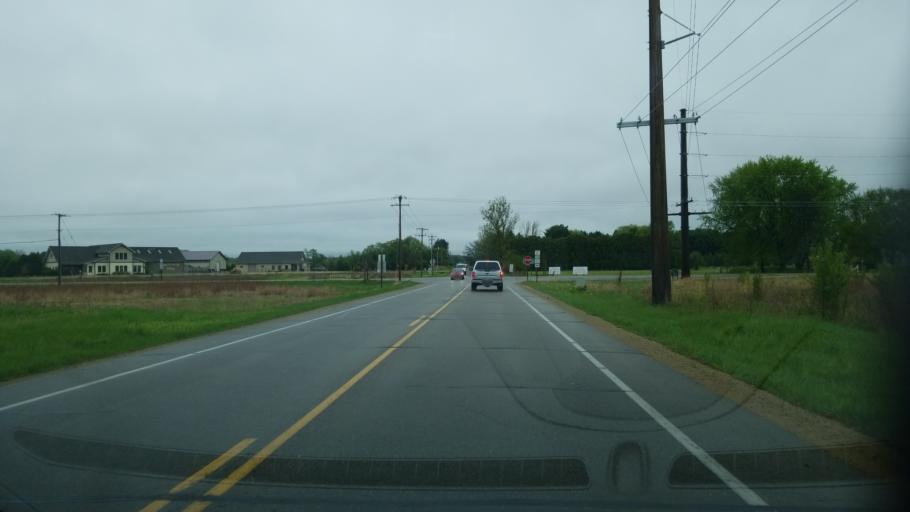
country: US
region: Wisconsin
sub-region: Dane County
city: Fitchburg
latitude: 42.9300
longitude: -89.4381
